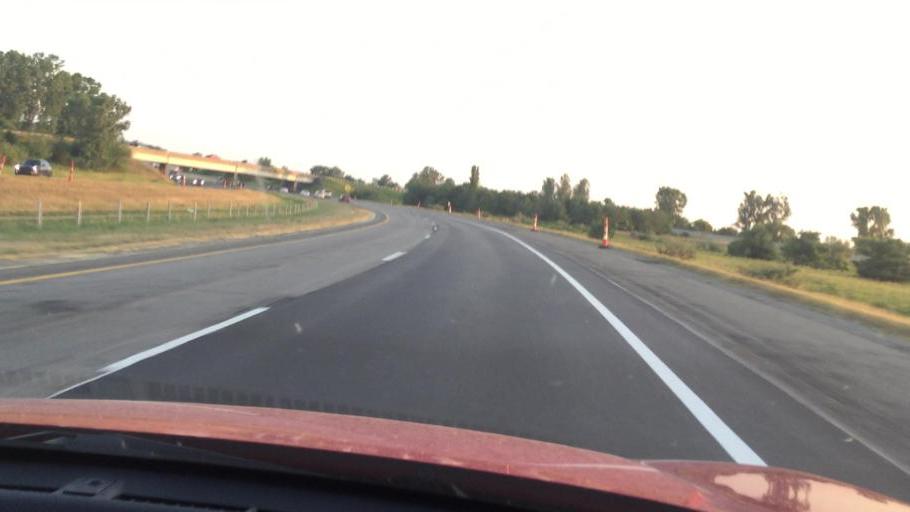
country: US
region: Michigan
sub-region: Washtenaw County
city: Milan
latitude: 42.0985
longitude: -83.6748
